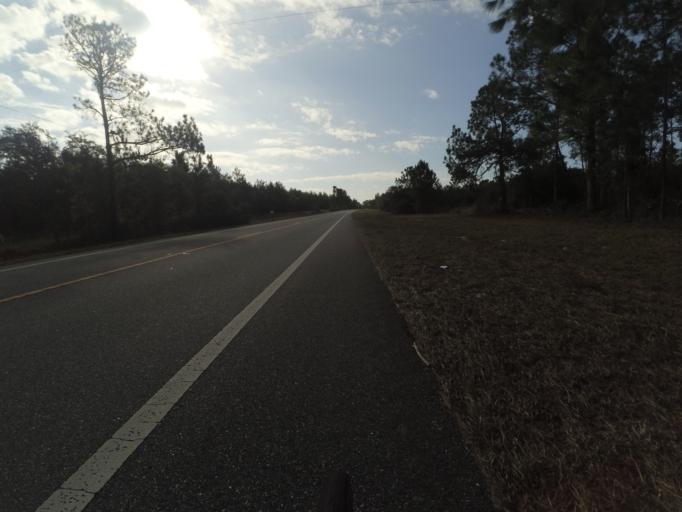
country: US
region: Florida
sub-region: Lake County
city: Astor
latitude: 29.1133
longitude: -81.6176
